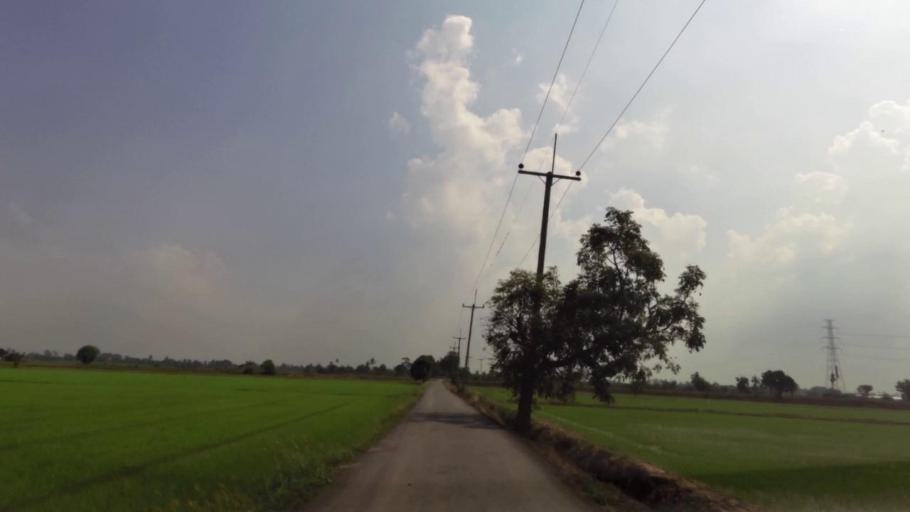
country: TH
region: Ang Thong
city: Pho Thong
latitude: 14.6196
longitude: 100.4002
